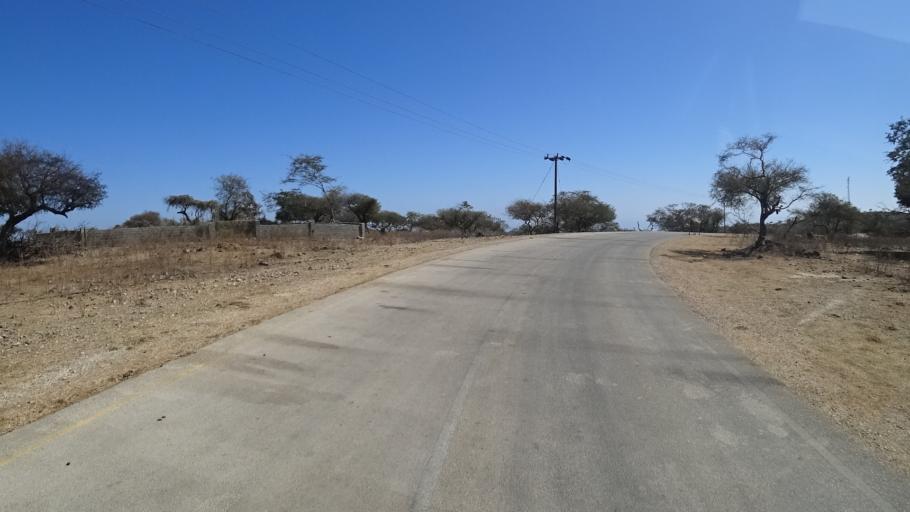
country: YE
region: Al Mahrah
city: Hawf
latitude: 16.7778
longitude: 53.3366
